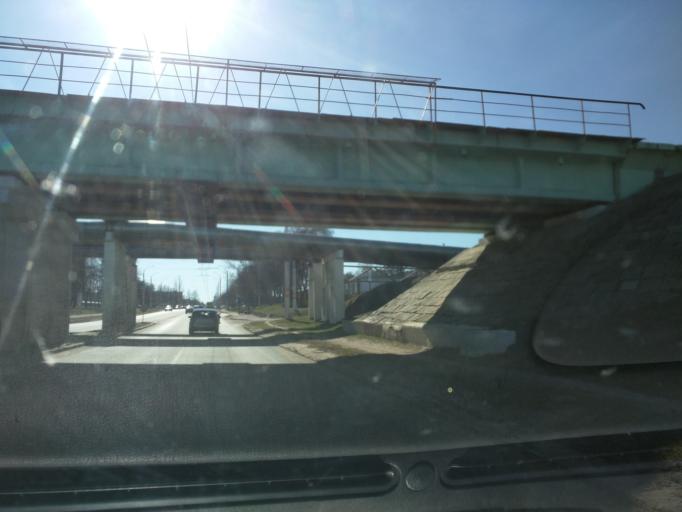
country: BY
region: Mogilev
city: Babruysk
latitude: 53.1819
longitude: 29.2092
